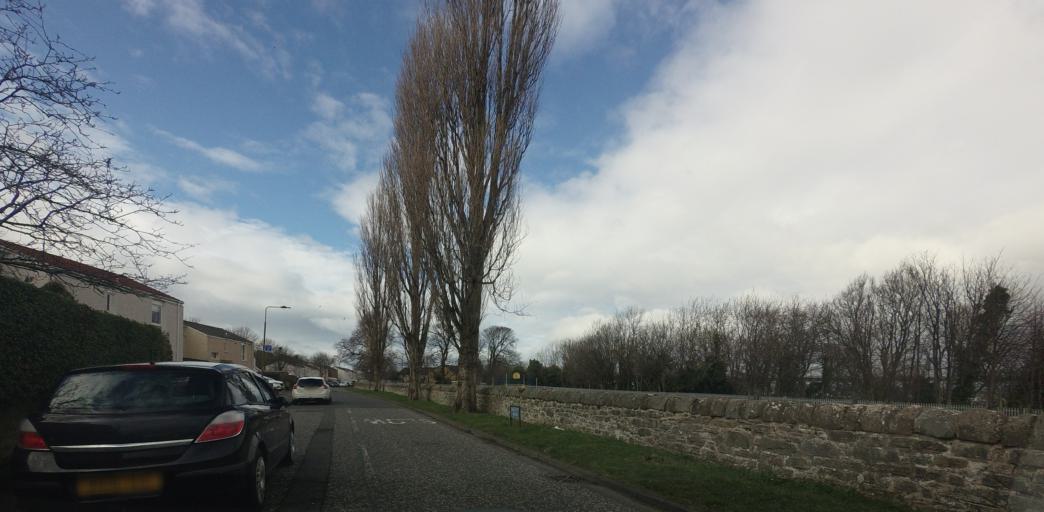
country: GB
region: Scotland
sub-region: Edinburgh
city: Queensferry
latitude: 55.9912
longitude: -3.4106
